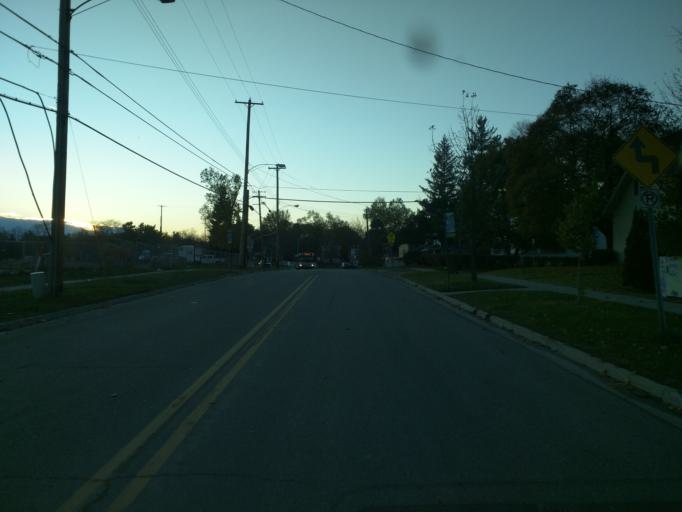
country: US
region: Michigan
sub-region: Ingham County
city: Lansing
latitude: 42.7488
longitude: -84.5614
